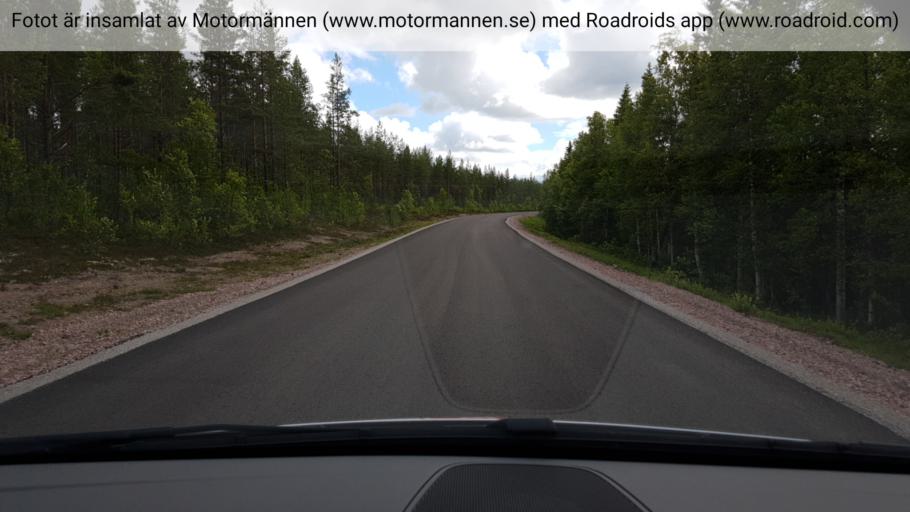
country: SE
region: Dalarna
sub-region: Alvdalens Kommun
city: AElvdalen
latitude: 61.6373
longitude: 14.1822
